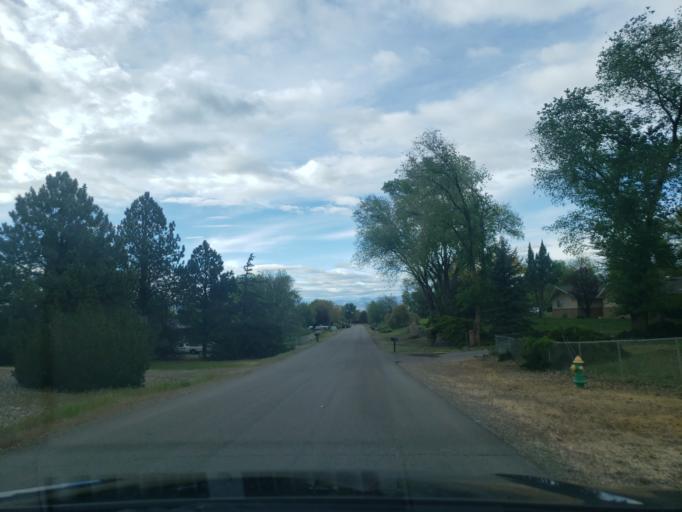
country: US
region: Colorado
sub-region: Mesa County
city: Redlands
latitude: 39.1001
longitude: -108.6615
